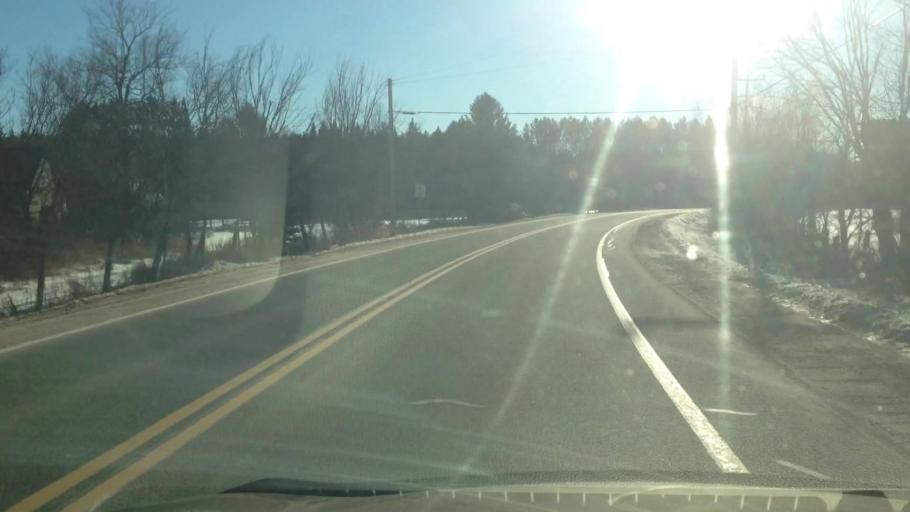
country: CA
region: Quebec
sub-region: Laurentides
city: Mont-Tremblant
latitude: 46.0079
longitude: -74.6159
